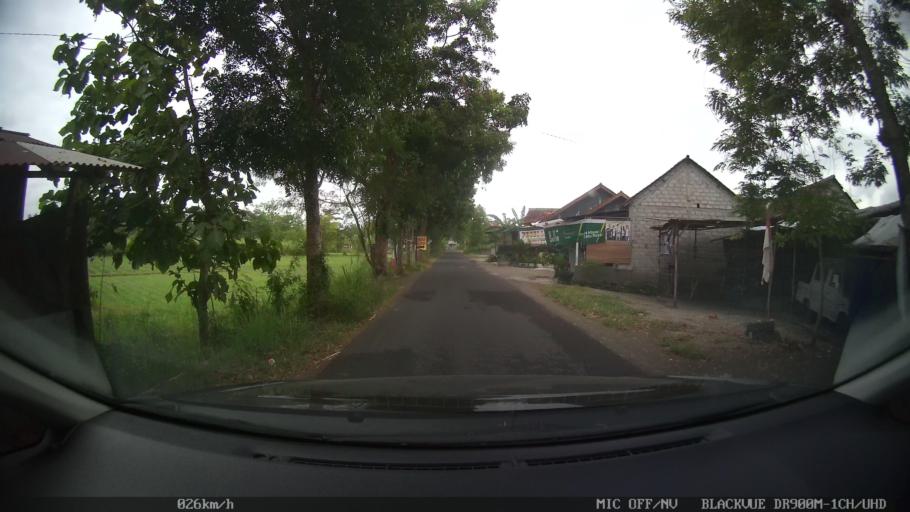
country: ID
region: Daerah Istimewa Yogyakarta
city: Sewon
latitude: -7.8631
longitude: 110.4020
